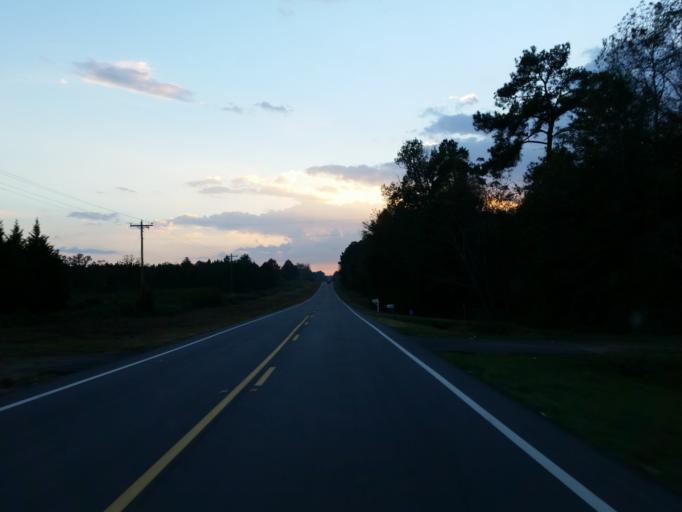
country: US
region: Georgia
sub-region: Pulaski County
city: Hawkinsville
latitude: 32.2321
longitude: -83.5110
